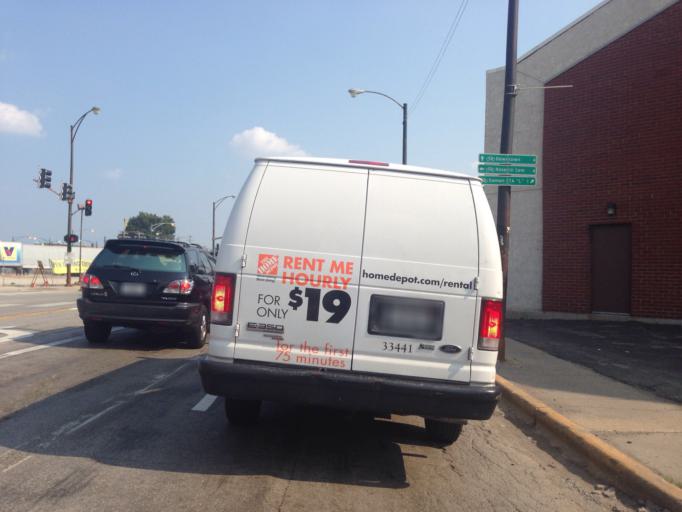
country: US
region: Illinois
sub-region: Cook County
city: Chicago
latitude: 41.9256
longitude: -87.6782
